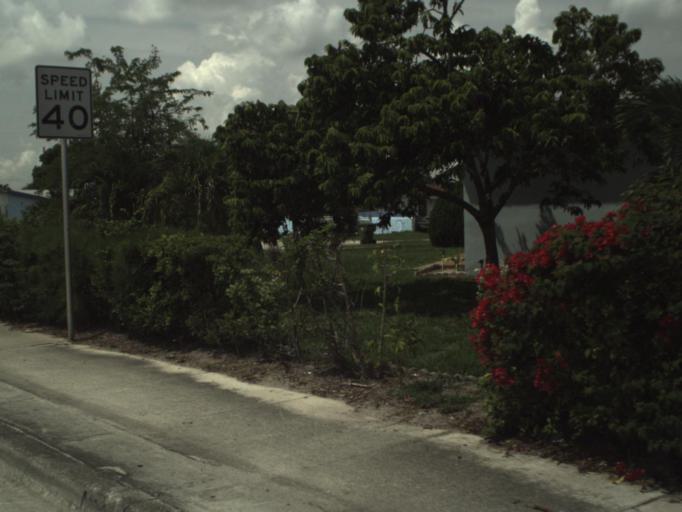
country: US
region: Florida
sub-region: Palm Beach County
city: Palm Springs
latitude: 26.6364
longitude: -80.0885
